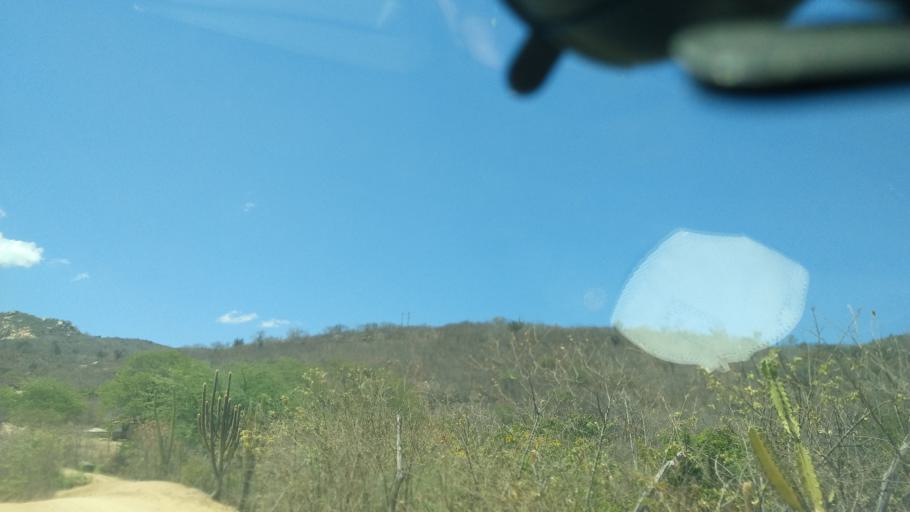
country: BR
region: Rio Grande do Norte
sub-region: Cerro Cora
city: Cerro Cora
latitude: -6.0155
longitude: -36.3112
